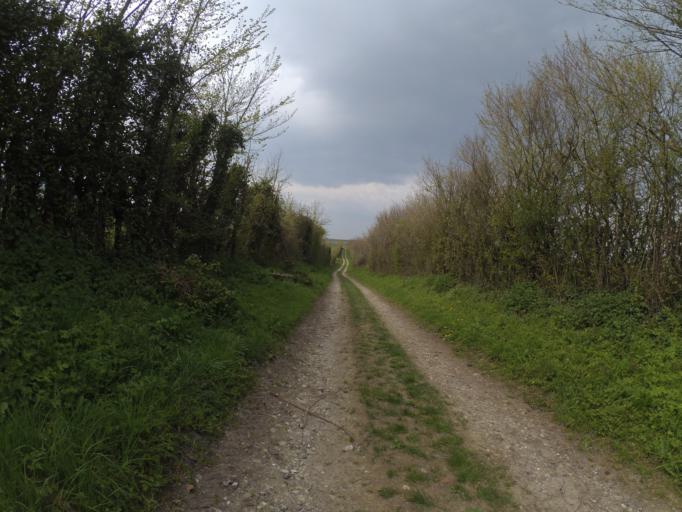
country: GB
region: England
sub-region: West Sussex
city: Arundel
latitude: 50.8748
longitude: -0.5278
